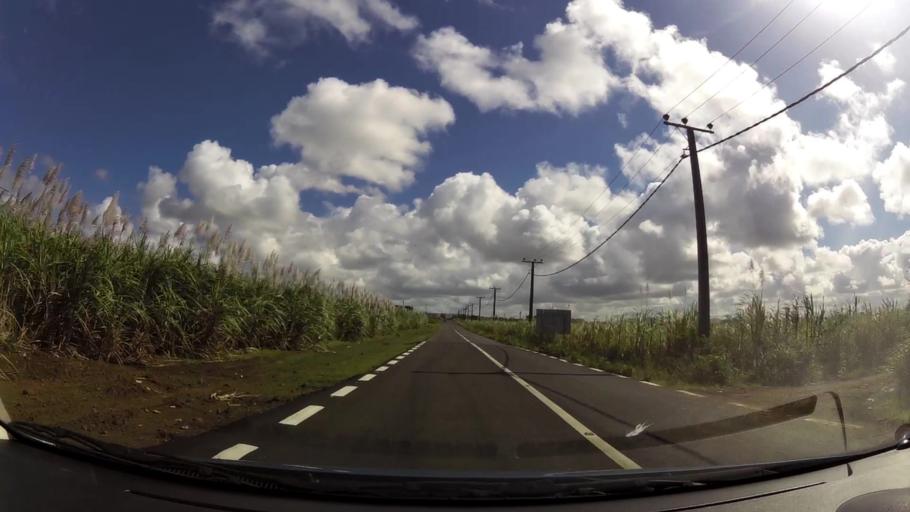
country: MU
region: Grand Port
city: Plaine Magnien
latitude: -20.4387
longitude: 57.6697
